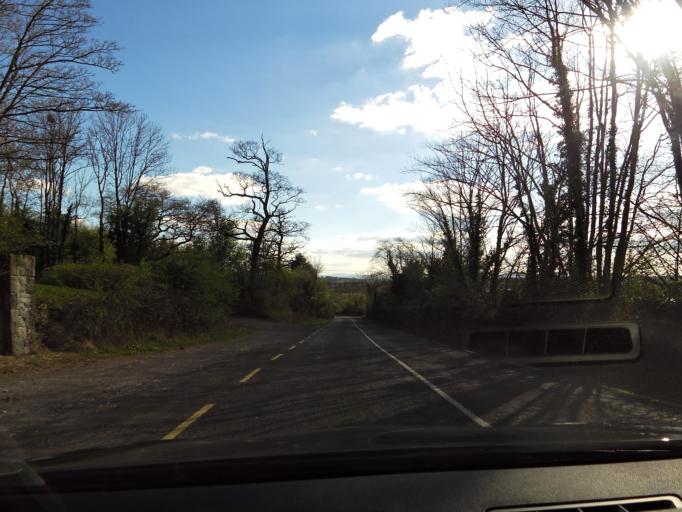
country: IE
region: Connaught
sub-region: County Galway
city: Portumna
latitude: 53.0968
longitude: -8.1814
